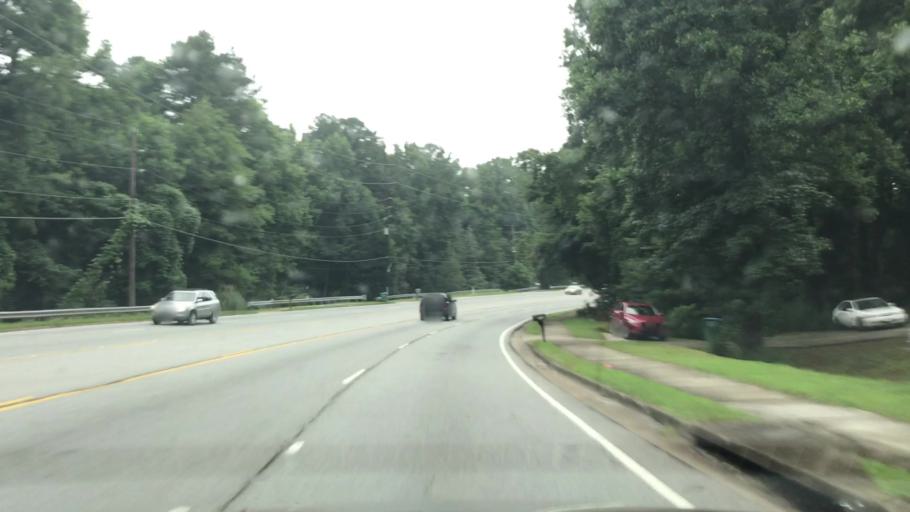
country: US
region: Georgia
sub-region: Gwinnett County
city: Norcross
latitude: 33.9380
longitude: -84.1682
